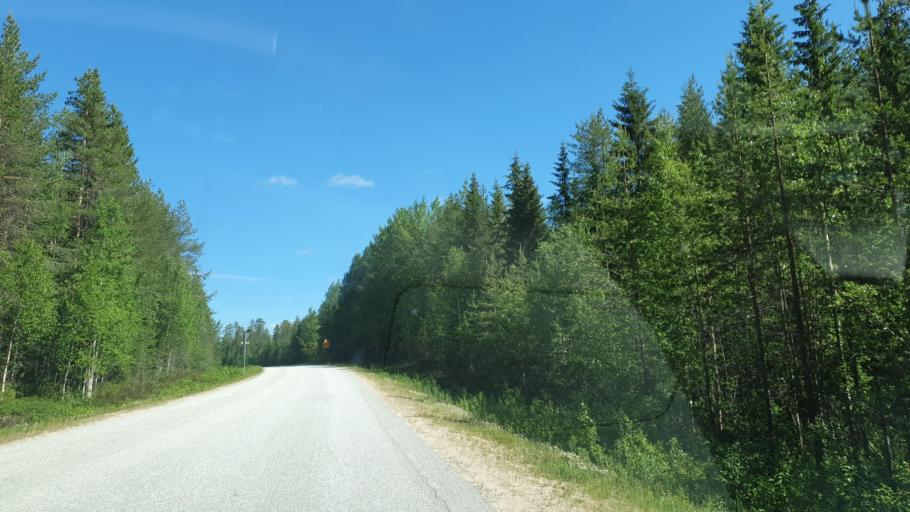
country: FI
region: Kainuu
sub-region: Kehys-Kainuu
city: Kuhmo
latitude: 64.4597
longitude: 29.5328
